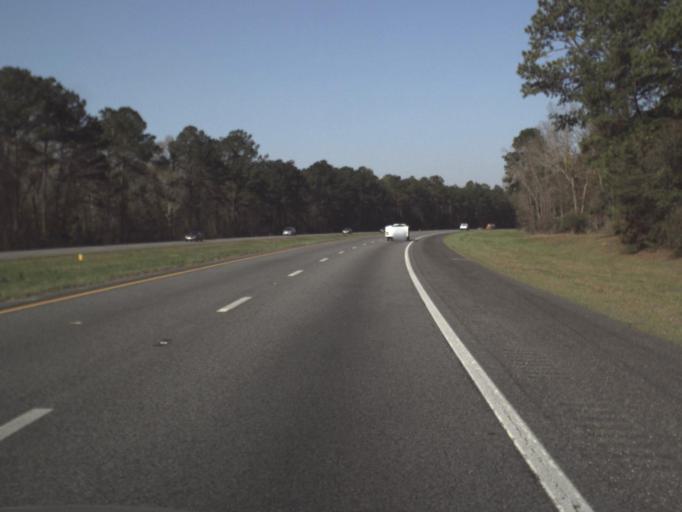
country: US
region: Florida
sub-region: Jefferson County
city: Monticello
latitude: 30.4787
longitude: -83.9363
